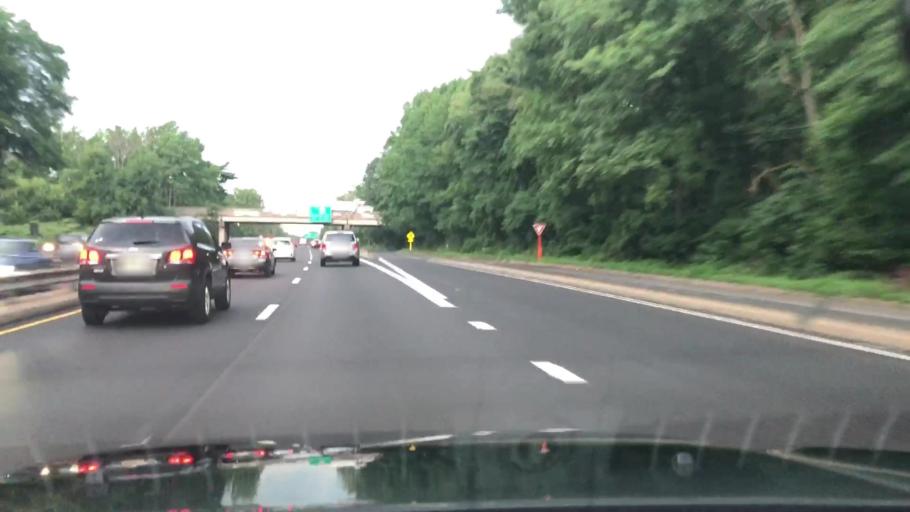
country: US
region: Pennsylvania
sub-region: Bucks County
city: Langhorne Manor
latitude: 40.1642
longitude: -74.9298
